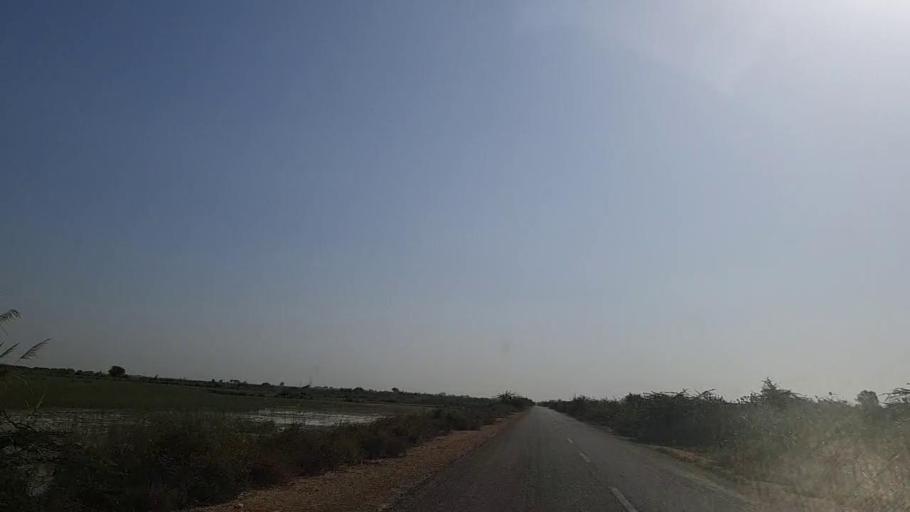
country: PK
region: Sindh
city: Jati
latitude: 24.4471
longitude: 68.2627
